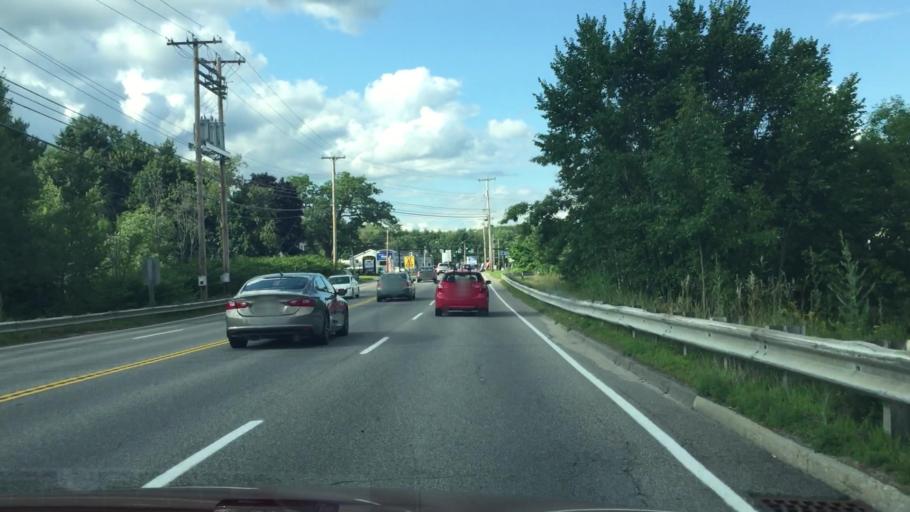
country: US
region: Maine
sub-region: York County
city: Saco
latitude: 43.5313
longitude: -70.4255
